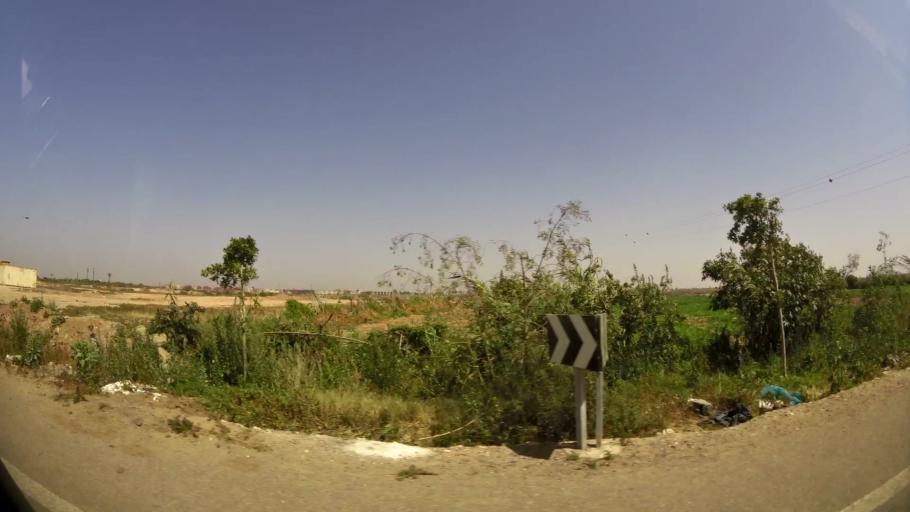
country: MA
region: Souss-Massa-Draa
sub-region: Inezgane-Ait Mellou
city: Inezgane
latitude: 30.3459
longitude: -9.5336
